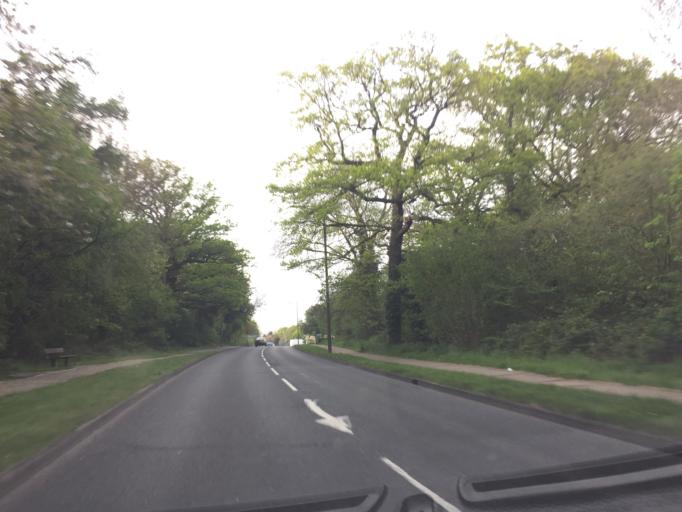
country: GB
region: England
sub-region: Essex
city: Harlow
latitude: 51.7731
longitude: 0.1128
